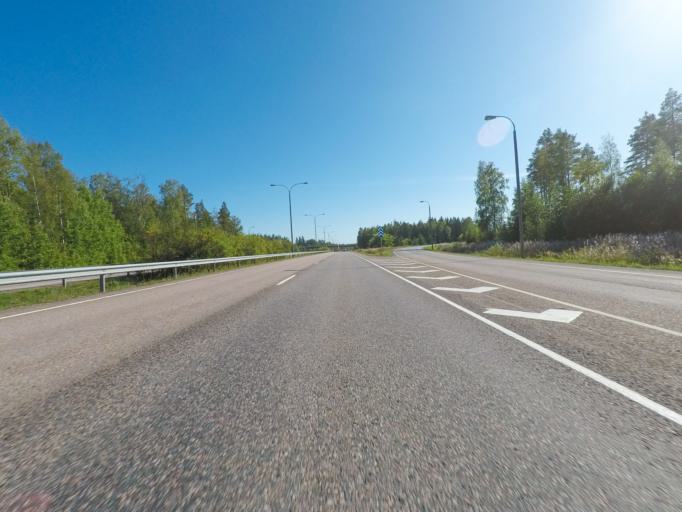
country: FI
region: Northern Savo
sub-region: Varkaus
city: Varkaus
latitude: 62.3078
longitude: 27.8575
